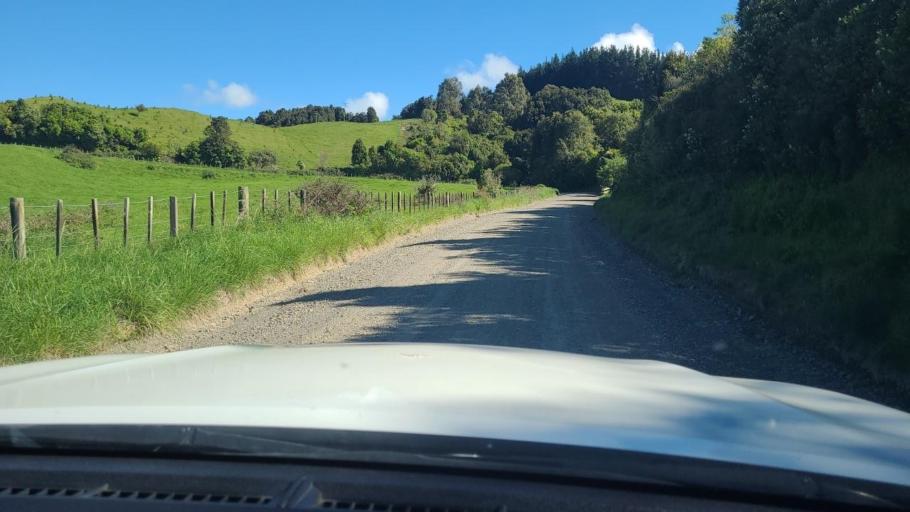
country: NZ
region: Hawke's Bay
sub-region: Napier City
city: Napier
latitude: -39.1521
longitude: 176.8409
